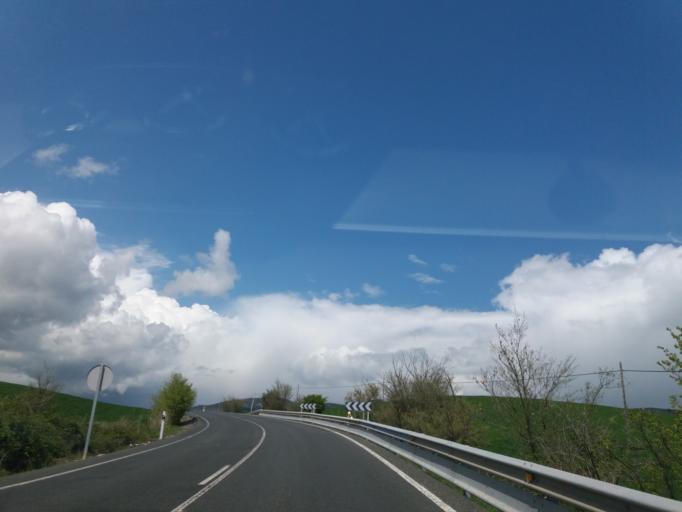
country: ES
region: La Rioja
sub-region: Provincia de La Rioja
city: Foncea
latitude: 42.5911
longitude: -3.0355
